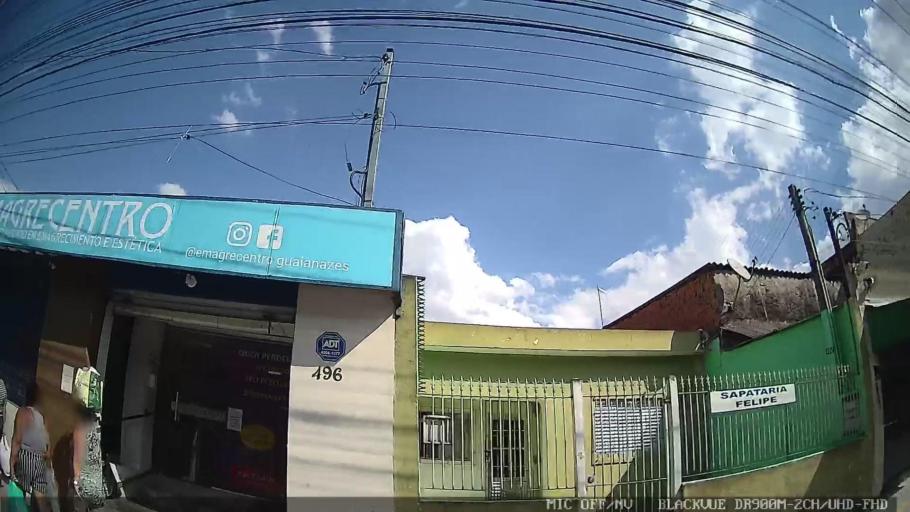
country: BR
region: Sao Paulo
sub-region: Ferraz De Vasconcelos
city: Ferraz de Vasconcelos
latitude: -23.5368
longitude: -46.4044
